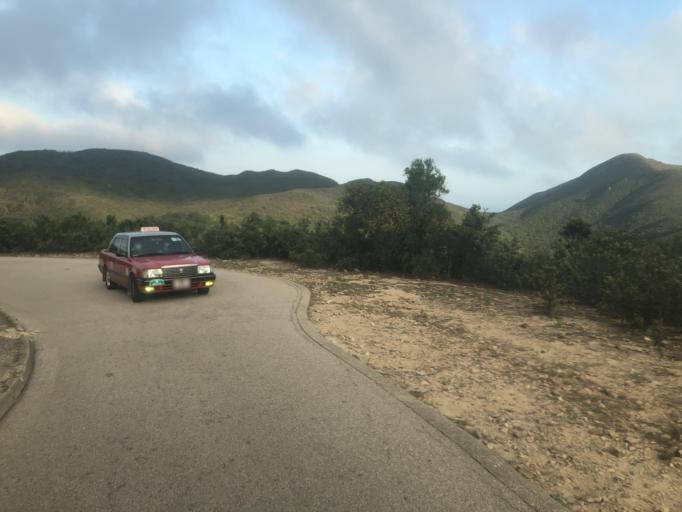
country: HK
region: Sai Kung
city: Sai Kung
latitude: 22.3614
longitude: 114.3513
